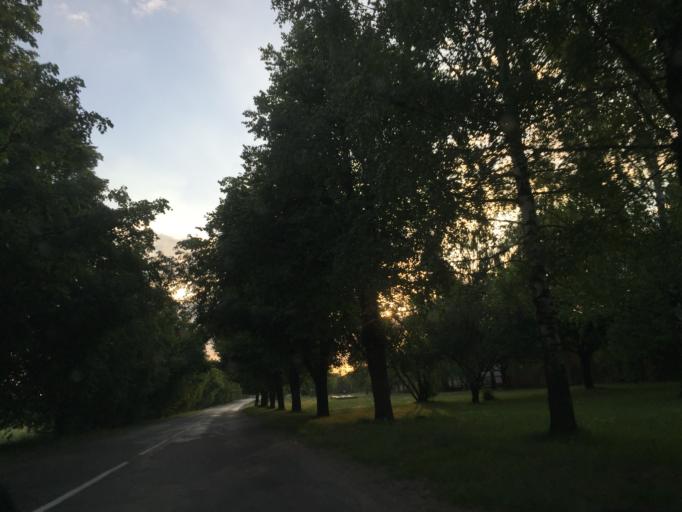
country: LV
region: Sigulda
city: Sigulda
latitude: 57.1405
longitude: 24.8666
